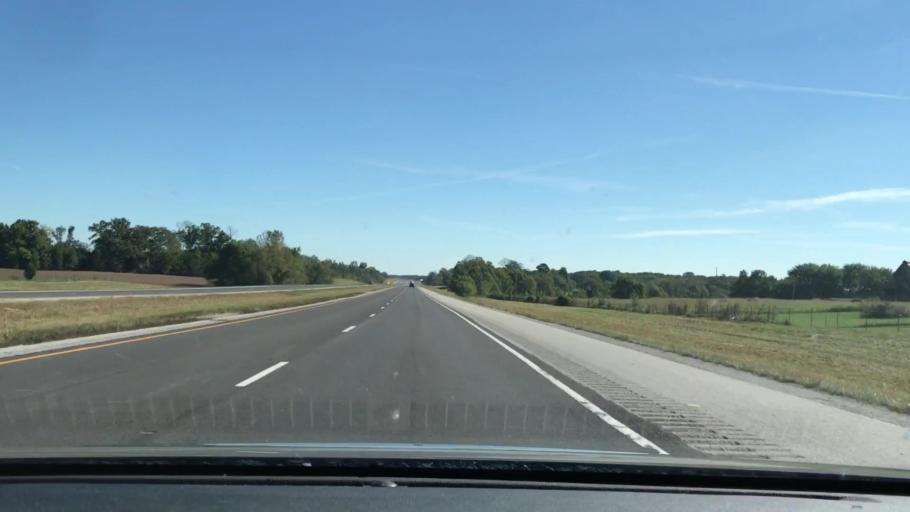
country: US
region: Kentucky
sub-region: Todd County
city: Elkton
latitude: 36.8028
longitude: -87.0878
